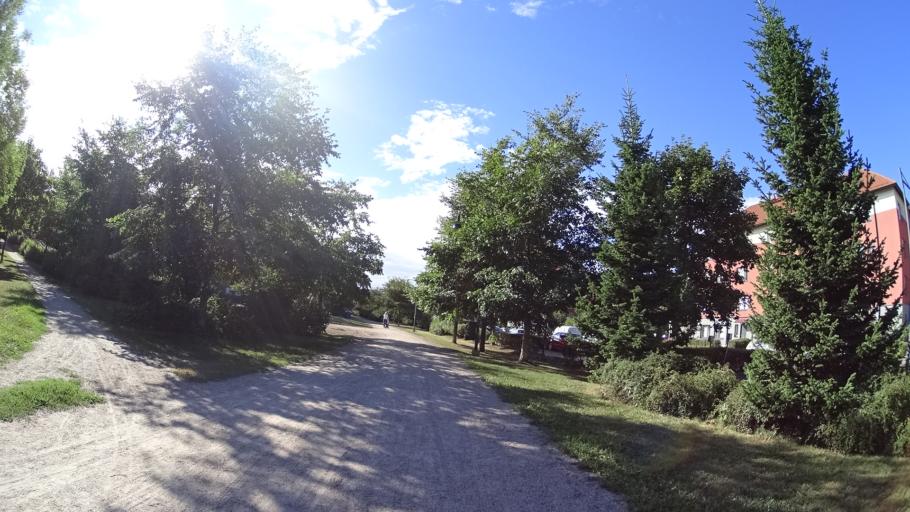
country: FI
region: Uusimaa
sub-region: Helsinki
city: Vantaa
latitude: 60.2831
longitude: 24.9634
